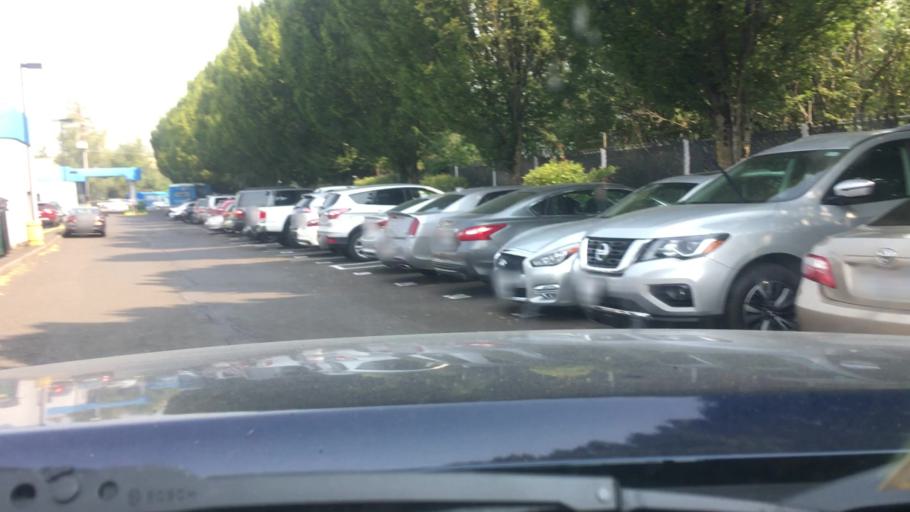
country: US
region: Oregon
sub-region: Multnomah County
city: Lents
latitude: 45.5669
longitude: -122.5512
